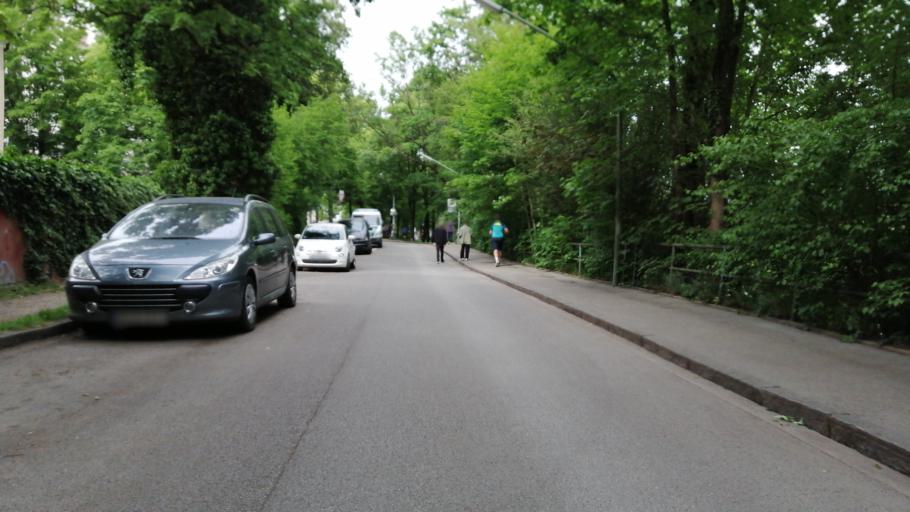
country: DE
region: Bavaria
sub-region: Upper Bavaria
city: Munich
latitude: 48.1204
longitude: 11.5629
